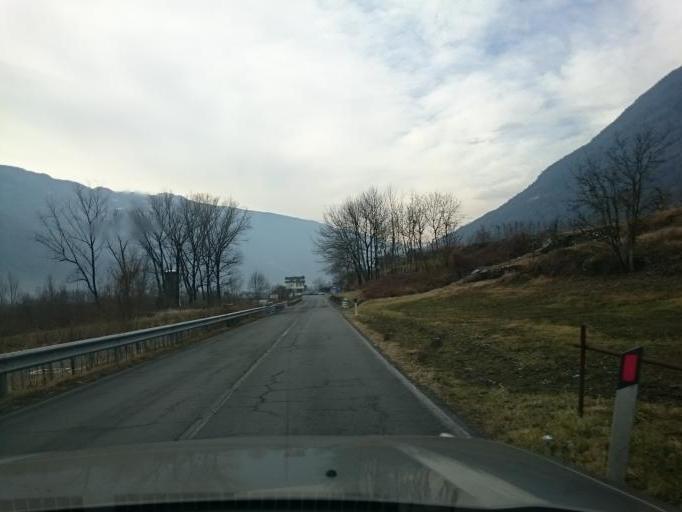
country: IT
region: Lombardy
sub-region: Provincia di Sondrio
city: Mazzo di Valtellina
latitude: 46.2637
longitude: 10.2525
